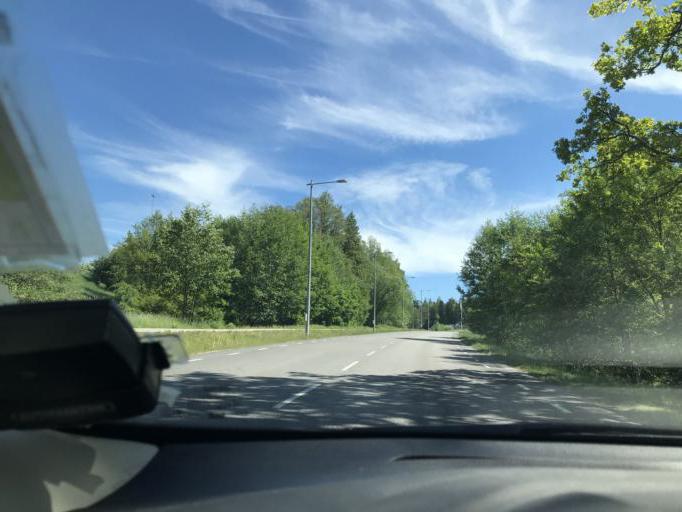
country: SE
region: Stockholm
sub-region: Botkyrka Kommun
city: Tumba
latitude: 59.2128
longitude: 17.8381
